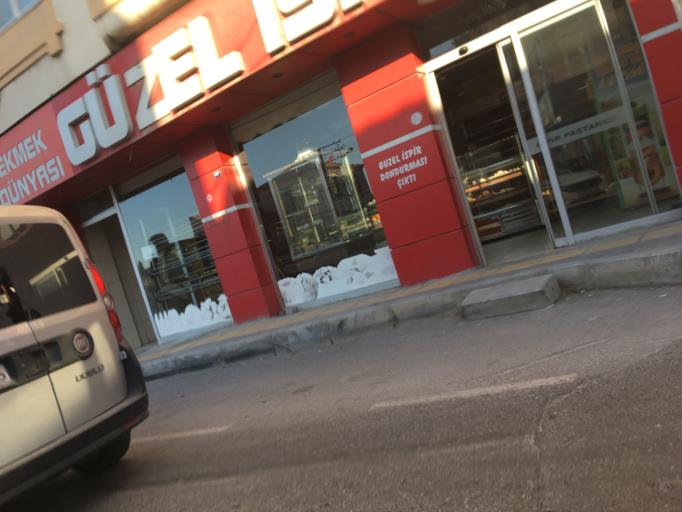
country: TR
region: Izmir
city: Buca
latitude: 38.3880
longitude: 27.1754
